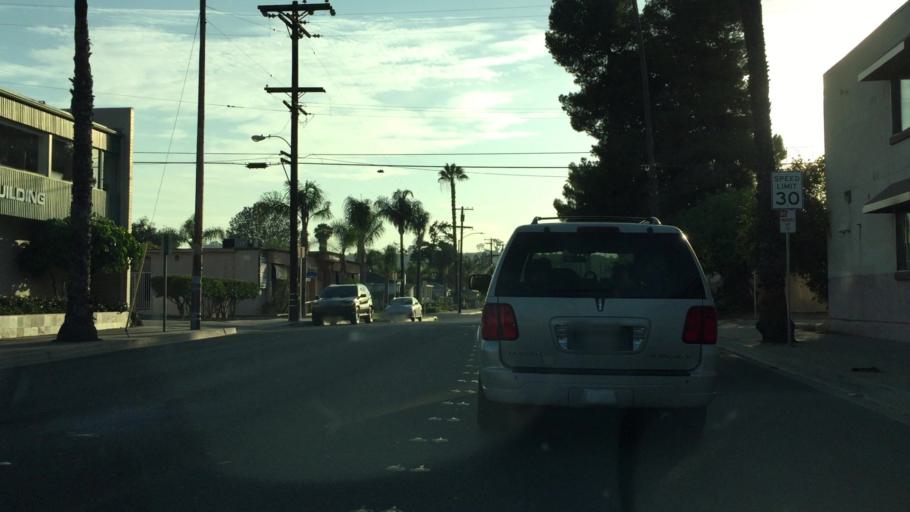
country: US
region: California
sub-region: San Diego County
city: El Cajon
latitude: 32.7928
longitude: -116.9627
